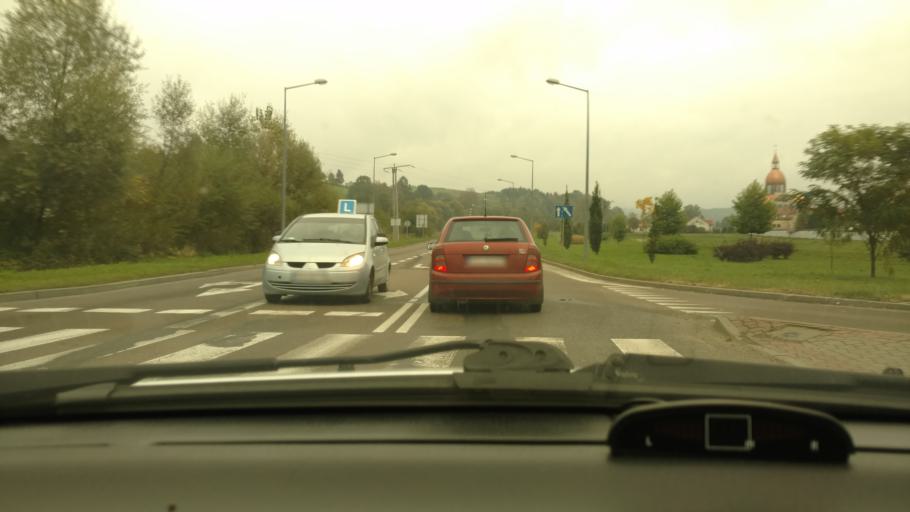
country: PL
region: Lesser Poland Voivodeship
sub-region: Powiat nowosadecki
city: Nowy Sacz
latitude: 49.6330
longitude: 20.7119
